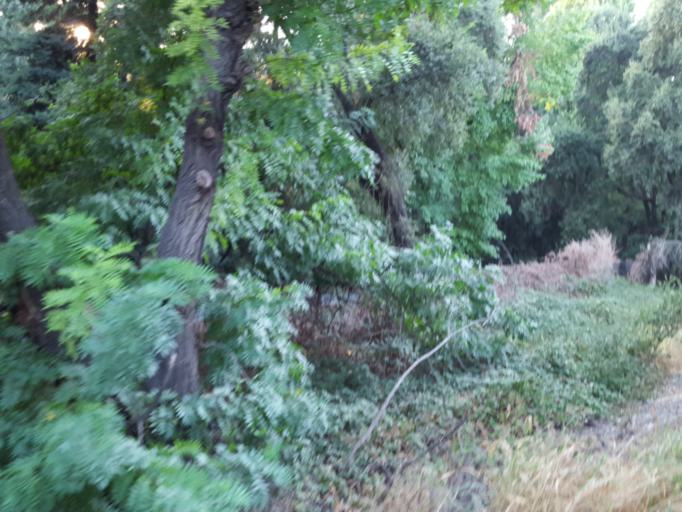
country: US
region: California
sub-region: Yolo County
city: West Sacramento
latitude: 38.5981
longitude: -121.5510
